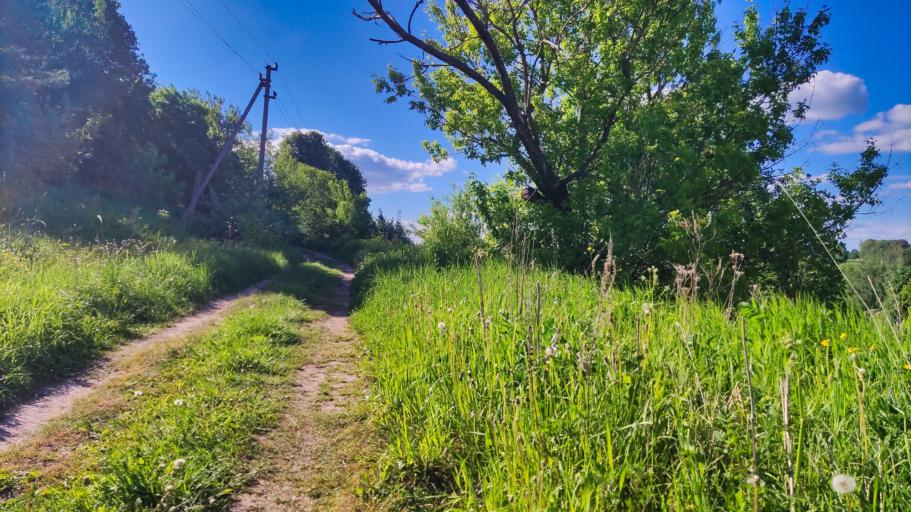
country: RU
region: Tverskaya
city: Rzhev
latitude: 56.2528
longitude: 34.3421
